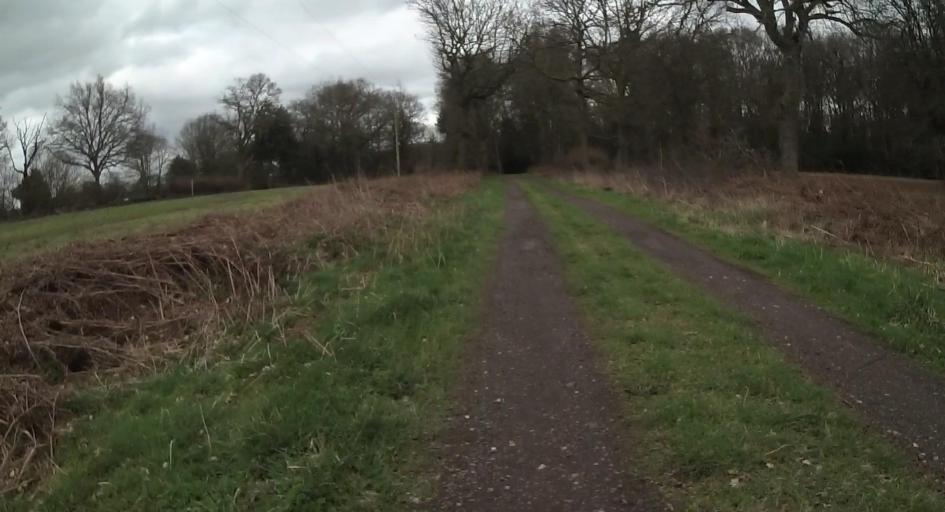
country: GB
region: England
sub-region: Hampshire
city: Old Basing
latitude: 51.1921
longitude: -1.0527
